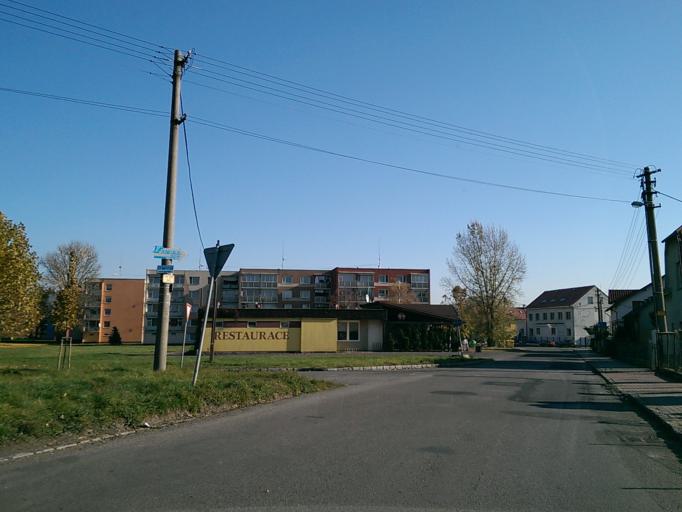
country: CZ
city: Prisovice
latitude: 50.5763
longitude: 15.0731
